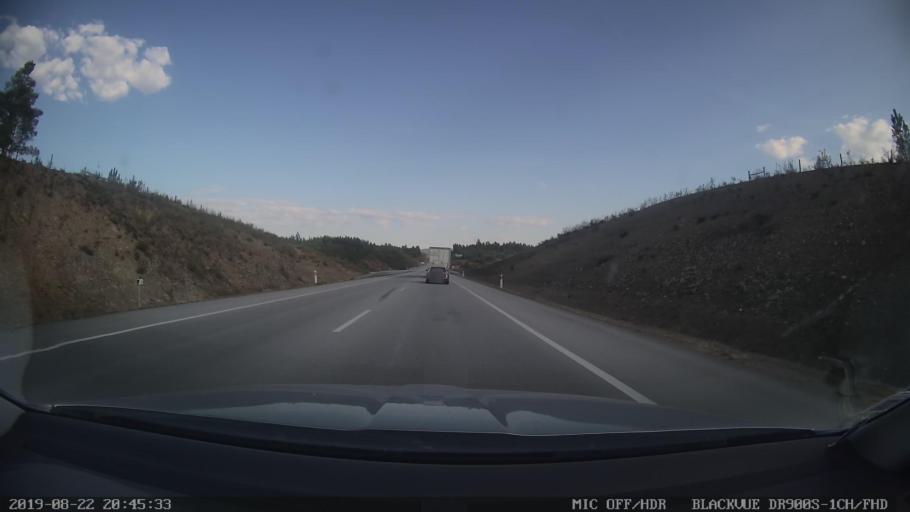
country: PT
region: Castelo Branco
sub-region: Proenca-A-Nova
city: Proenca-a-Nova
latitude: 39.7174
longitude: -7.8671
